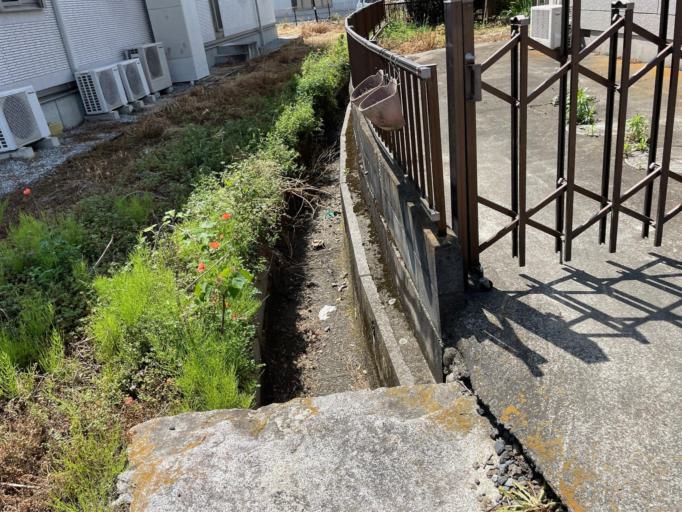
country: JP
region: Tochigi
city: Ashikaga
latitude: 36.3052
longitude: 139.4205
